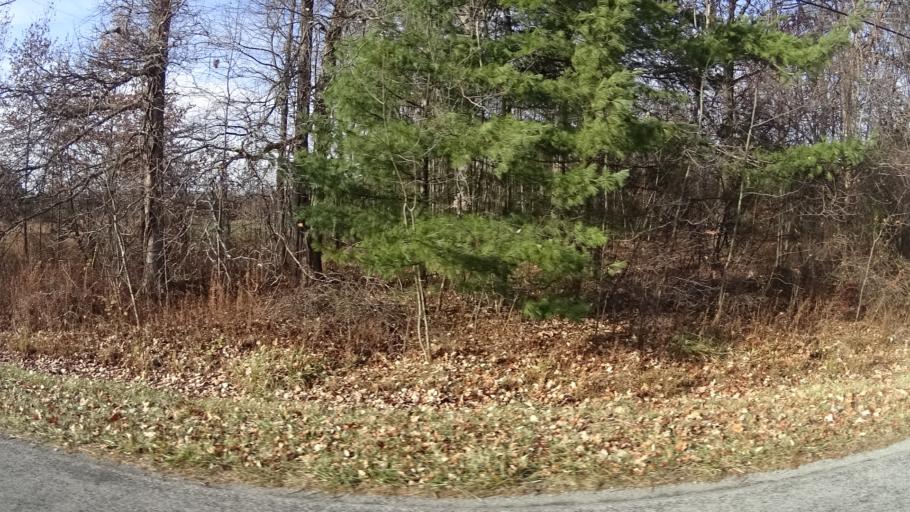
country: US
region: Ohio
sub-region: Lorain County
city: Lagrange
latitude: 41.2051
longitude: -82.0629
